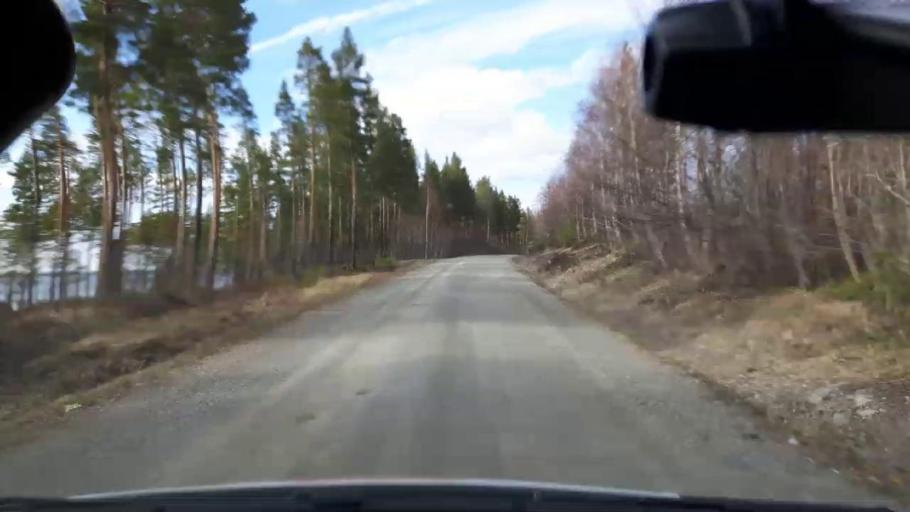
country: SE
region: Jaemtland
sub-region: Bergs Kommun
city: Hoverberg
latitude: 62.7356
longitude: 14.6636
